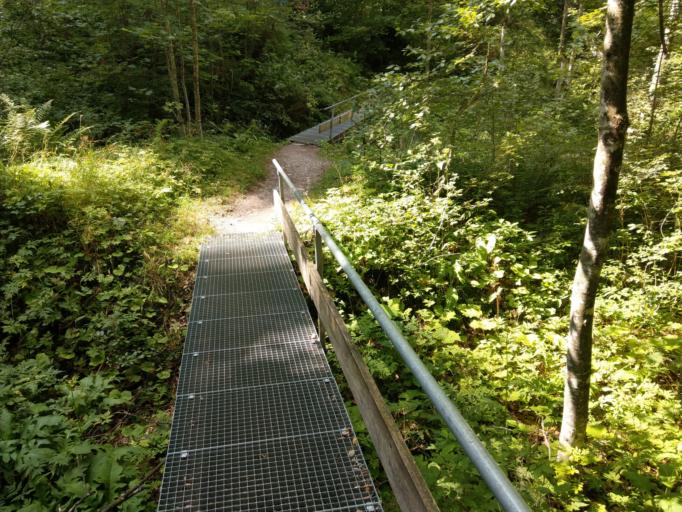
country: DE
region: Bavaria
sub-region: Swabia
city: Nesselwang
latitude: 47.6107
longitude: 10.5016
